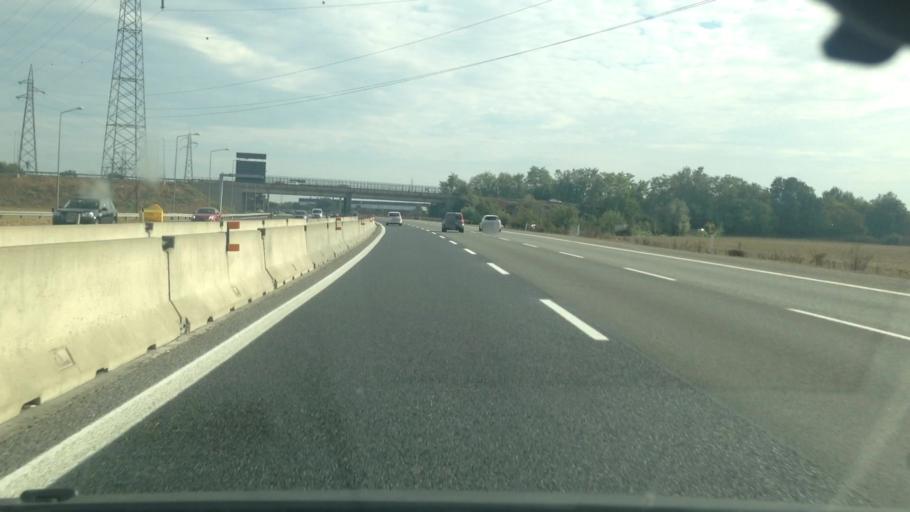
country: IT
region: Piedmont
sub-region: Provincia di Torino
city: Nichelino
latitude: 44.9954
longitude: 7.6263
